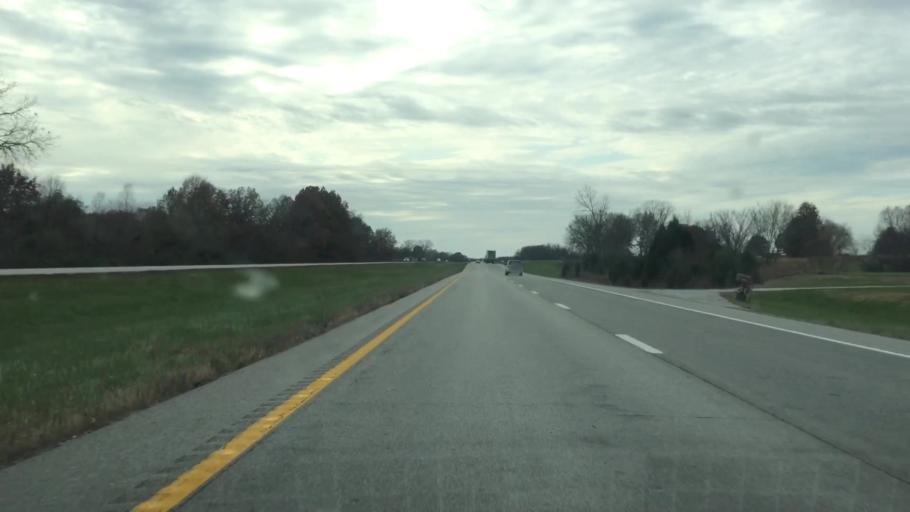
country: US
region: Missouri
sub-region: Cass County
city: Garden City
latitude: 38.5175
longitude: -94.1219
